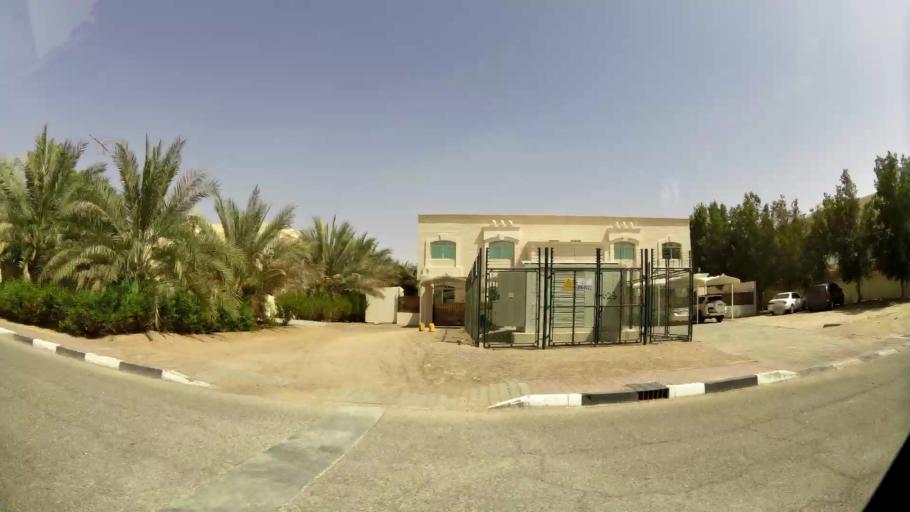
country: AE
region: Abu Dhabi
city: Al Ain
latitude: 24.2253
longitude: 55.7026
